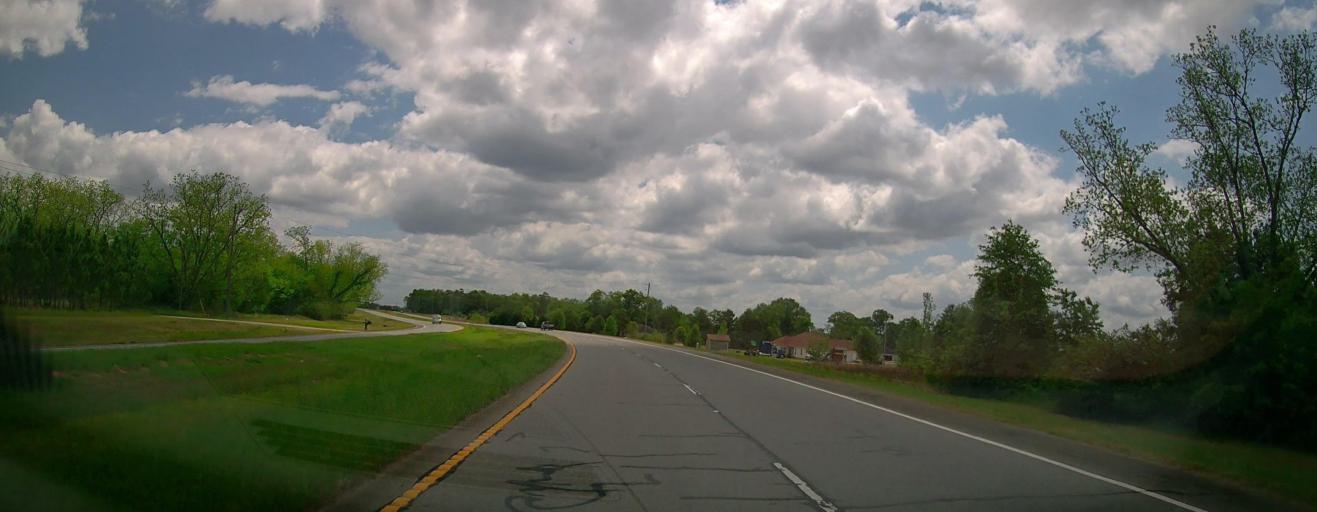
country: US
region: Georgia
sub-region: Laurens County
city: Dublin
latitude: 32.6025
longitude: -82.9749
